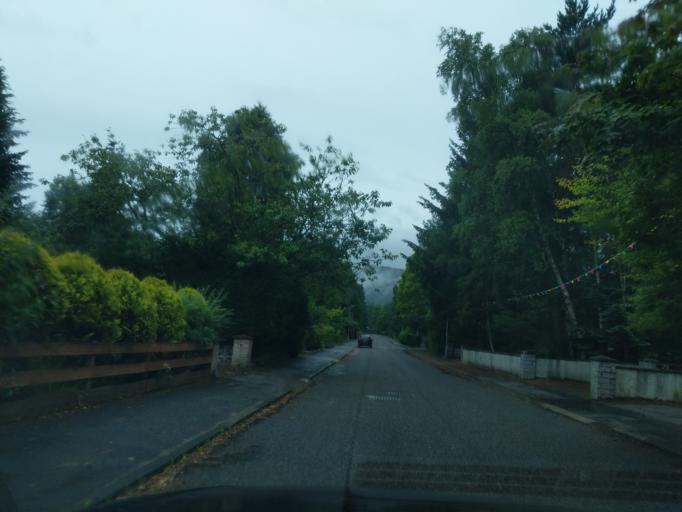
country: GB
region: Scotland
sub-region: Aberdeenshire
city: Aboyne
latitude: 57.0748
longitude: -2.7995
